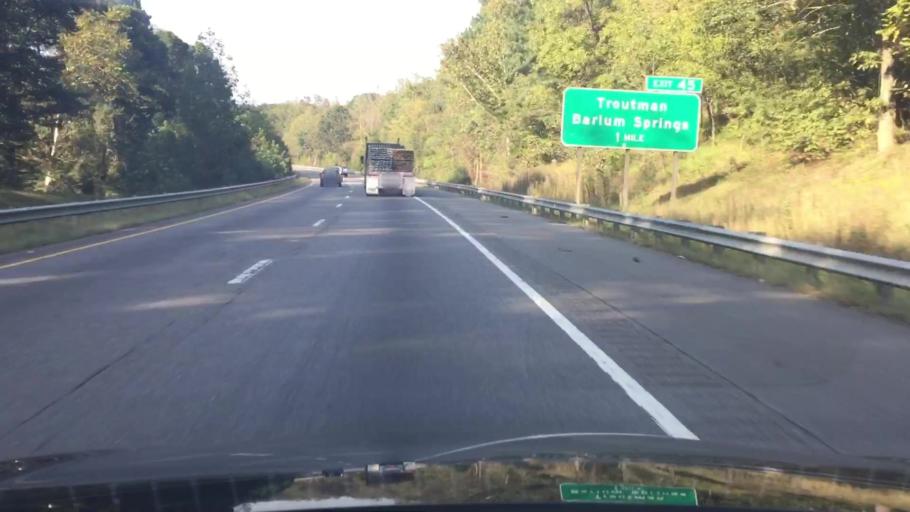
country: US
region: North Carolina
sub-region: Iredell County
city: Troutman
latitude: 35.7086
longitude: -80.8554
